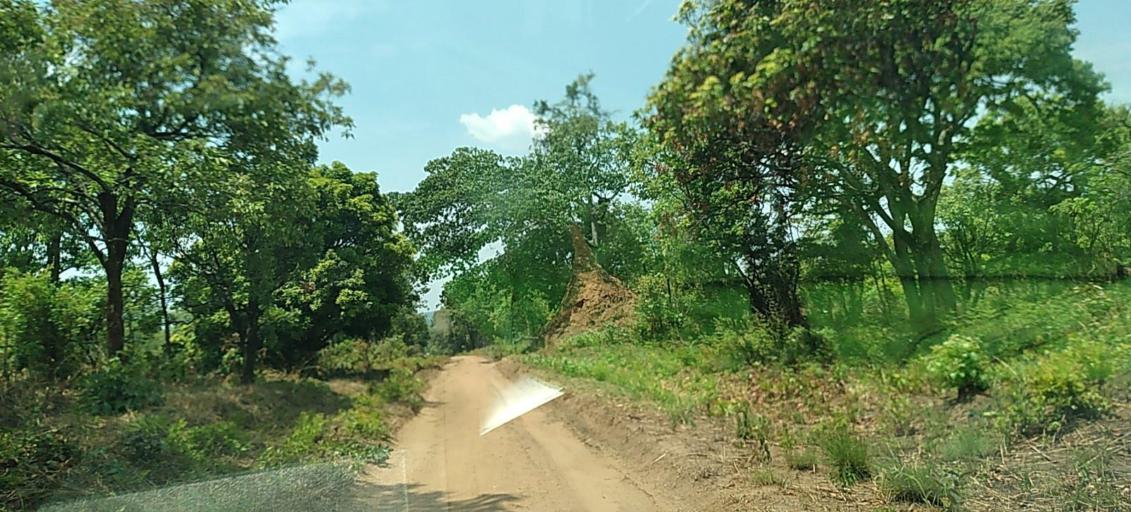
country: CD
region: Katanga
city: Kolwezi
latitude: -11.3175
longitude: 25.2332
